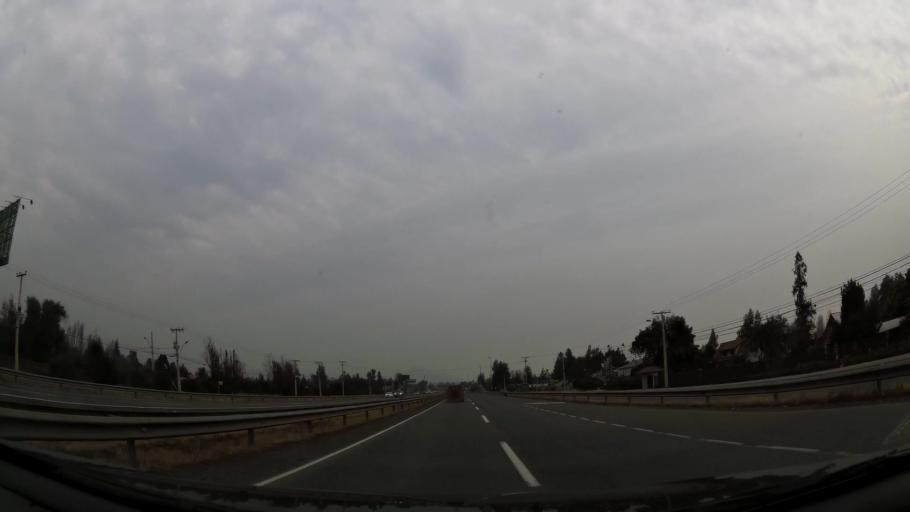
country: CL
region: Santiago Metropolitan
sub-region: Provincia de Chacabuco
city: Chicureo Abajo
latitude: -33.2479
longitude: -70.6979
